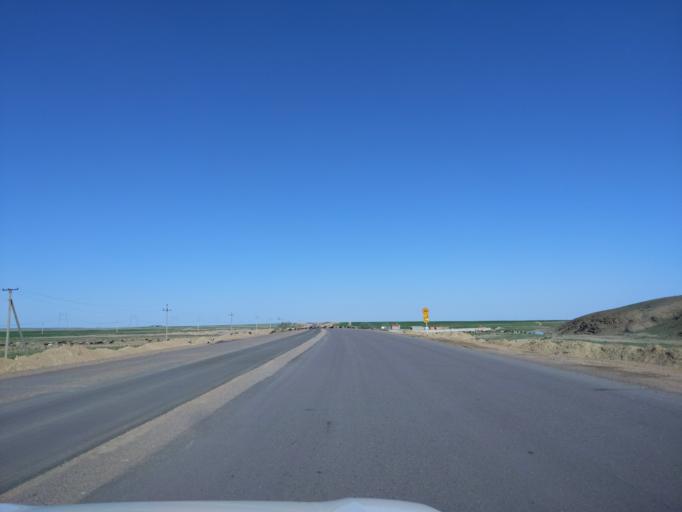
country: KZ
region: Almaty Oblysy
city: Bakanas
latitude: 44.0939
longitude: 75.9873
